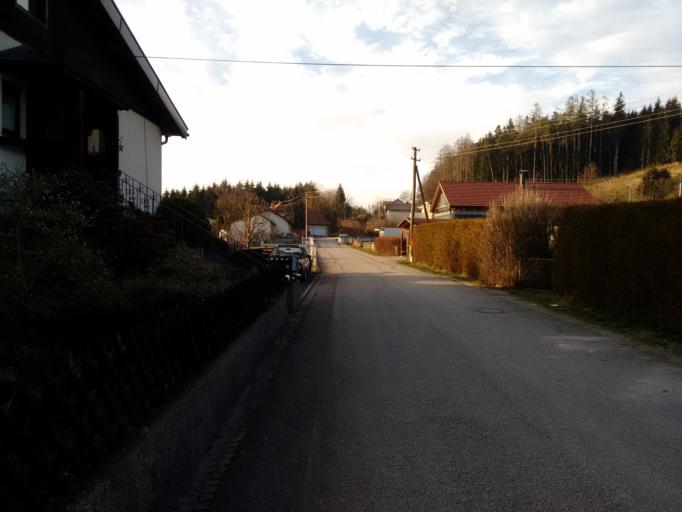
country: AT
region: Upper Austria
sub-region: Politischer Bezirk Grieskirchen
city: Bad Schallerbach
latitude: 48.1947
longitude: 13.9674
